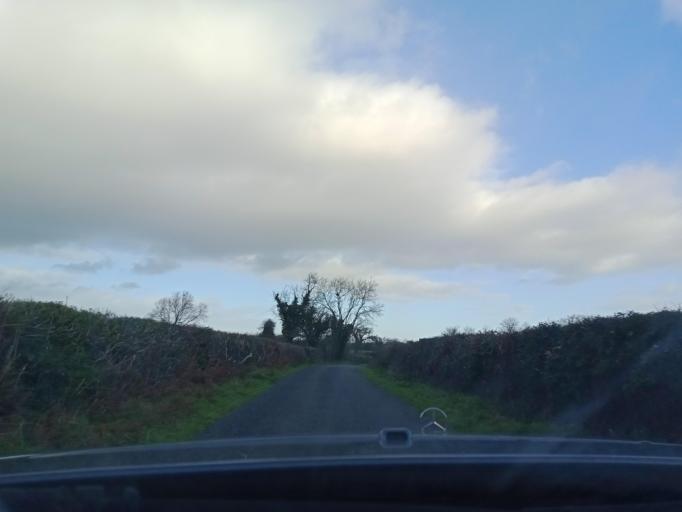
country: IE
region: Leinster
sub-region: Kilkenny
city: Callan
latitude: 52.4731
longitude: -7.3830
